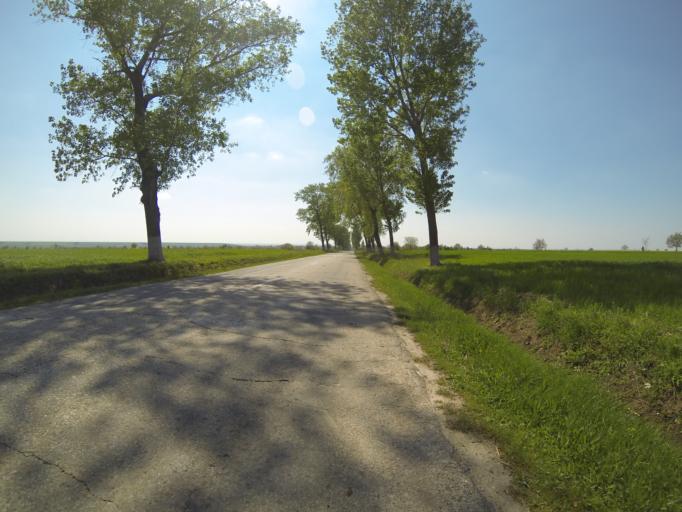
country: RO
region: Dolj
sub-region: Comuna Caraula
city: Caraula
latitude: 44.1990
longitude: 23.2736
